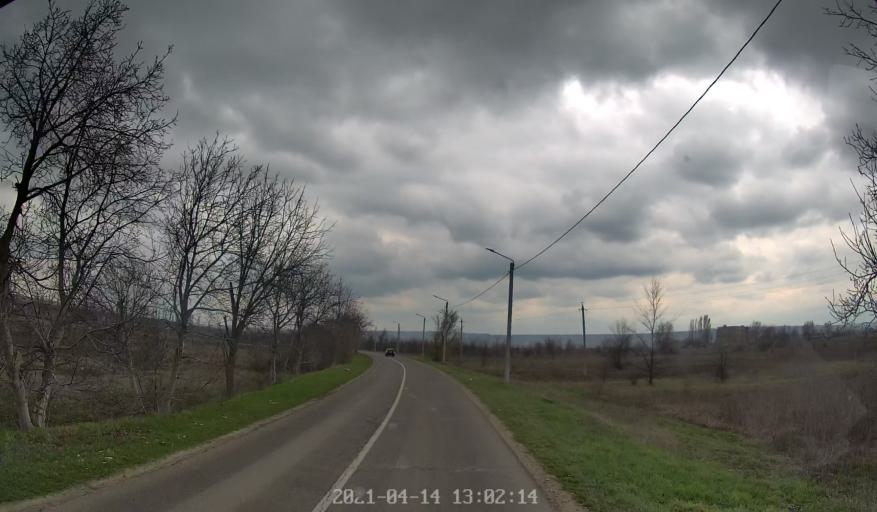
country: MD
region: Chisinau
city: Vadul lui Voda
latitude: 47.1252
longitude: 29.1113
